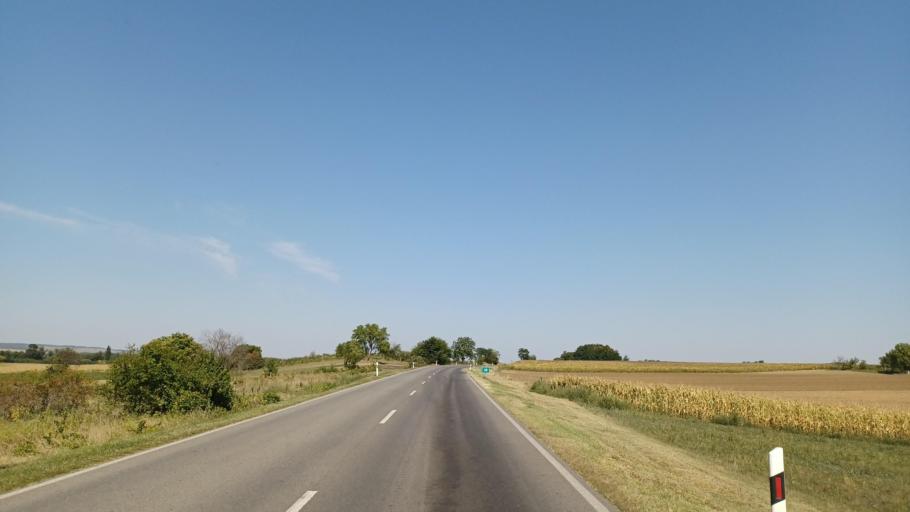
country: HU
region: Tolna
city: Nagydorog
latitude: 46.6425
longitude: 18.6498
